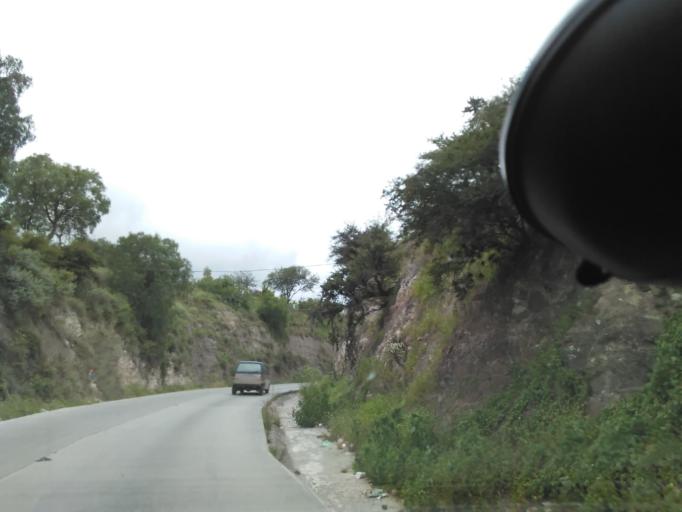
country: MX
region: Hidalgo
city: Tula de Allende
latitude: 20.0591
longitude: -99.3513
